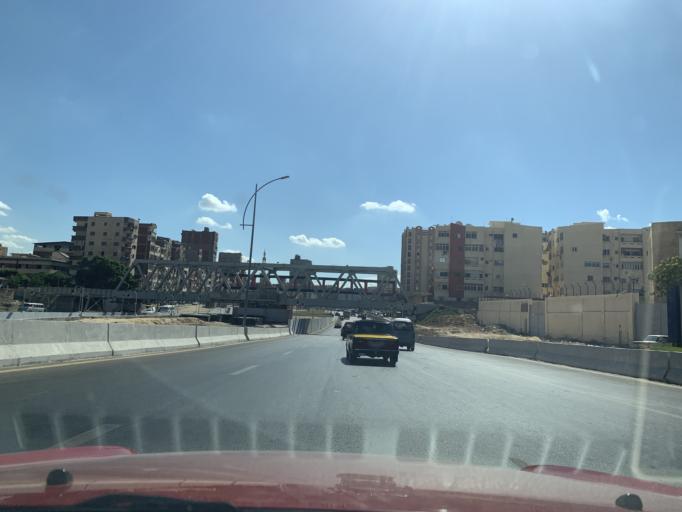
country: EG
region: Alexandria
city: Alexandria
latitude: 31.2184
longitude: 29.9637
